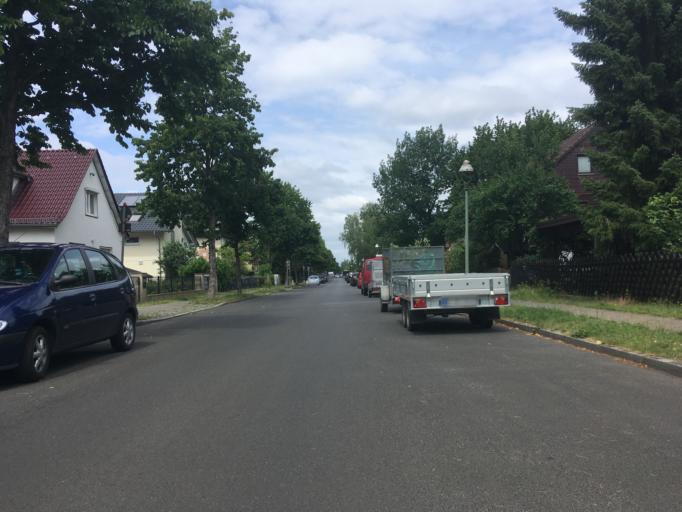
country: DE
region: Berlin
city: Lichtenrade
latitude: 52.4081
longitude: 13.3917
